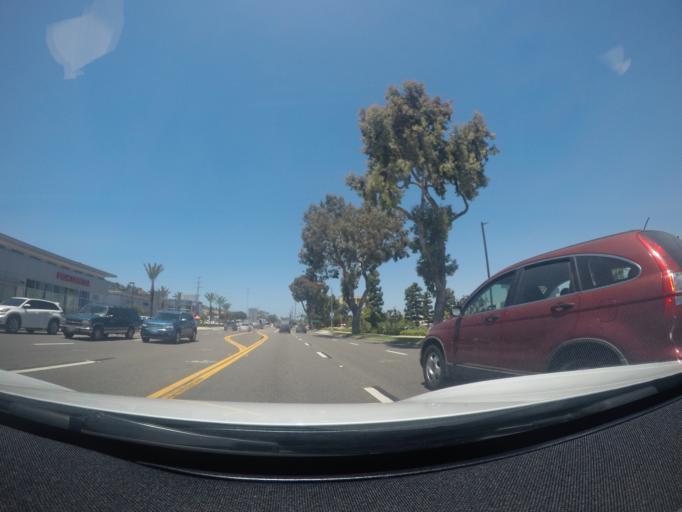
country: US
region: California
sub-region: Los Angeles County
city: Rolling Hills Estates
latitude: 33.8044
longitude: -118.3493
